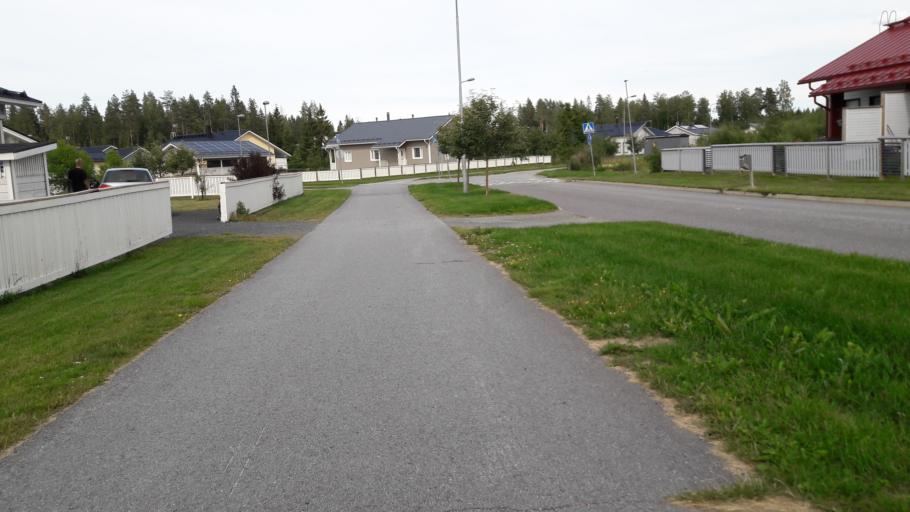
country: FI
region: North Karelia
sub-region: Joensuu
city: Joensuu
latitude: 62.5721
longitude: 29.8244
